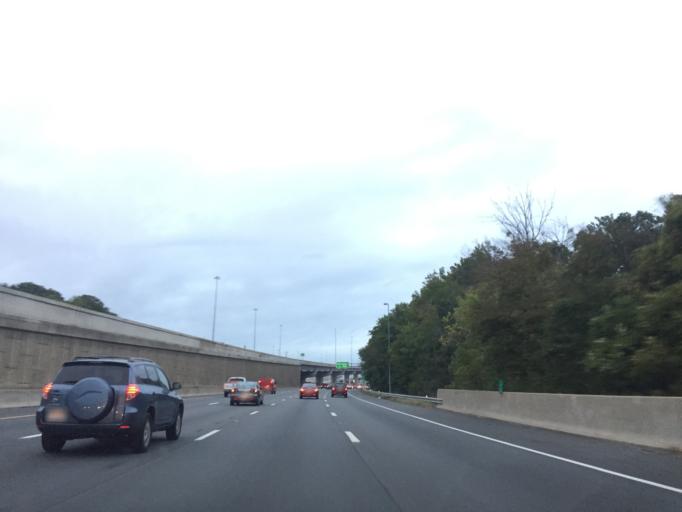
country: US
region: Virginia
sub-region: Fairfax County
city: Franconia
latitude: 38.7920
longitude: -77.1616
